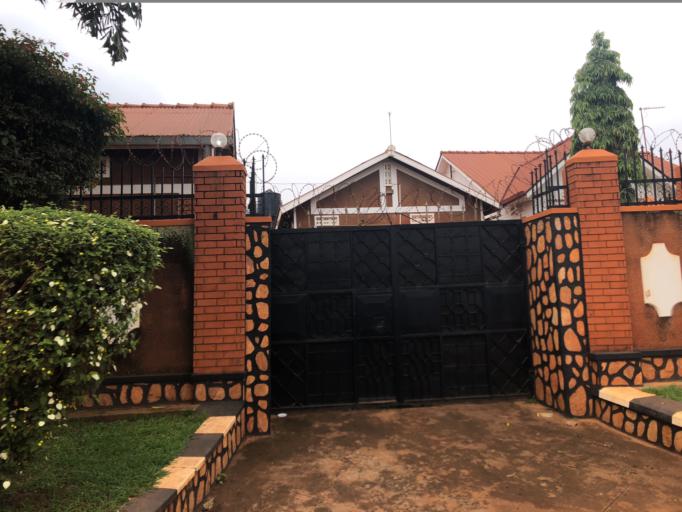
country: UG
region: Central Region
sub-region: Mukono District
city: Mukono
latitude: 0.3538
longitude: 32.7505
